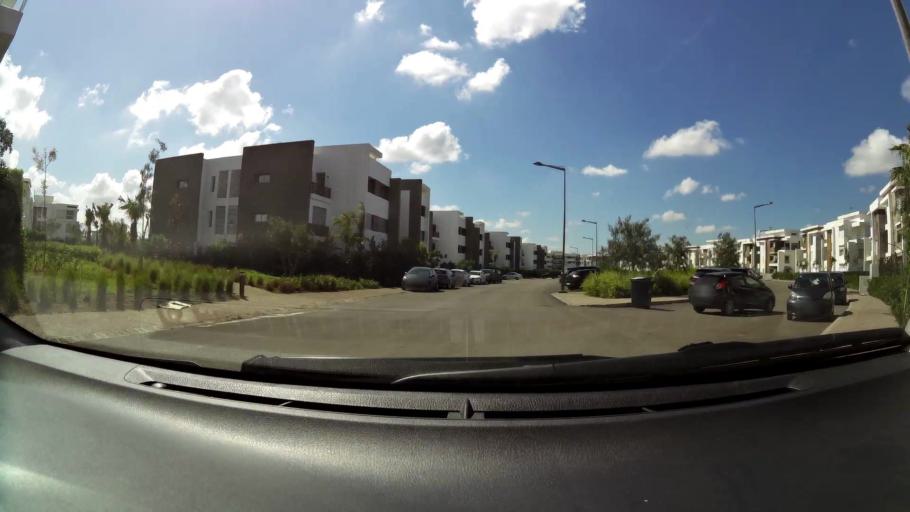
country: MA
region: Grand Casablanca
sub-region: Nouaceur
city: Bouskoura
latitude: 33.4731
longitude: -7.6016
